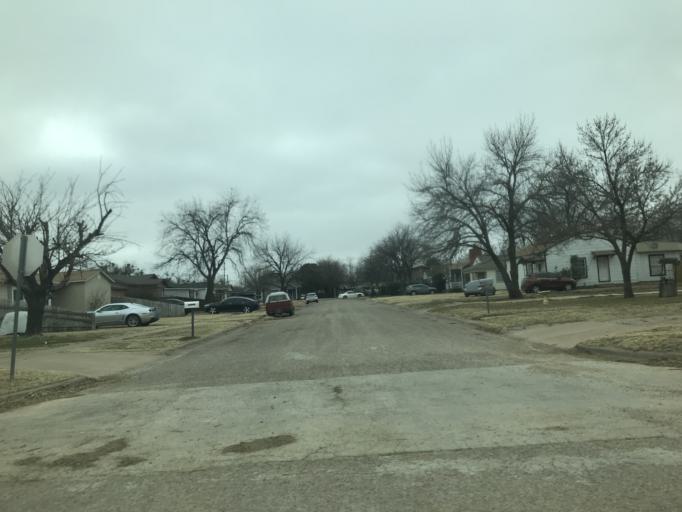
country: US
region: Texas
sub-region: Taylor County
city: Abilene
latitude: 32.4268
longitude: -99.7560
